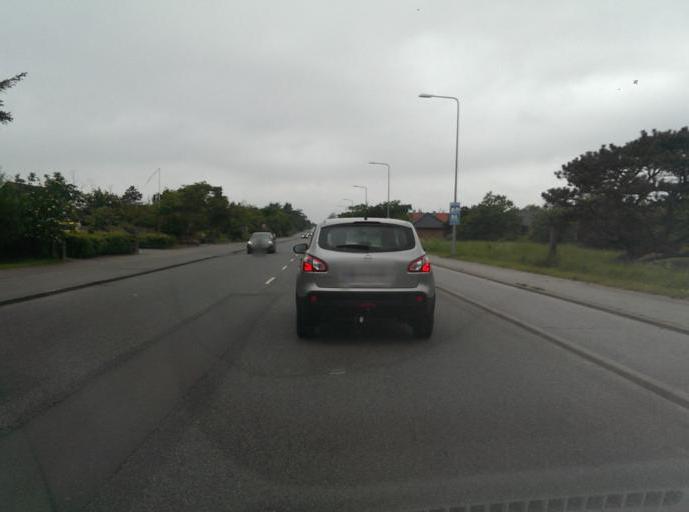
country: DK
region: South Denmark
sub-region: Fano Kommune
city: Nordby
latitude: 55.5122
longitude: 8.3783
